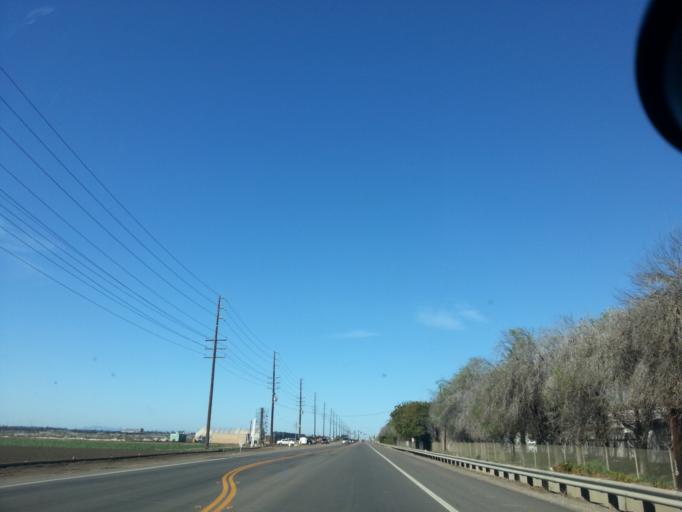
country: US
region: California
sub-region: Ventura County
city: Camarillo
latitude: 34.2057
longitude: -119.0769
